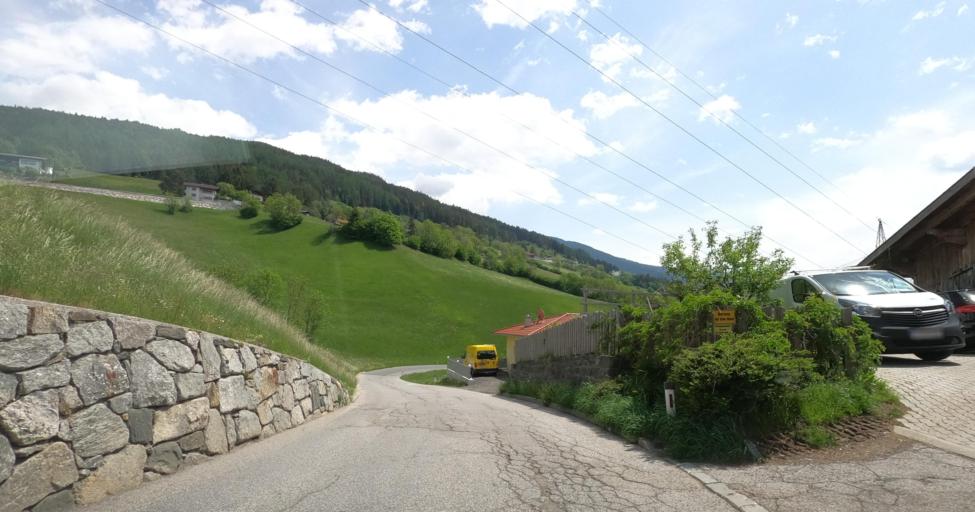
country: AT
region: Tyrol
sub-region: Politischer Bezirk Innsbruck Land
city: Schoenberg im Stubaital
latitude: 47.1810
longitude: 11.4352
